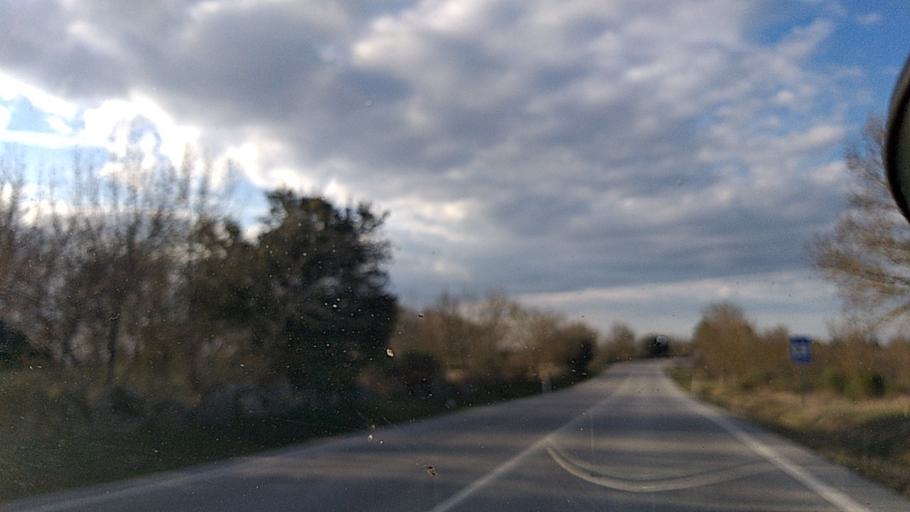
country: ES
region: Castille and Leon
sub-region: Provincia de Salamanca
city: Aldea del Obispo
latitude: 40.6865
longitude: -6.8751
